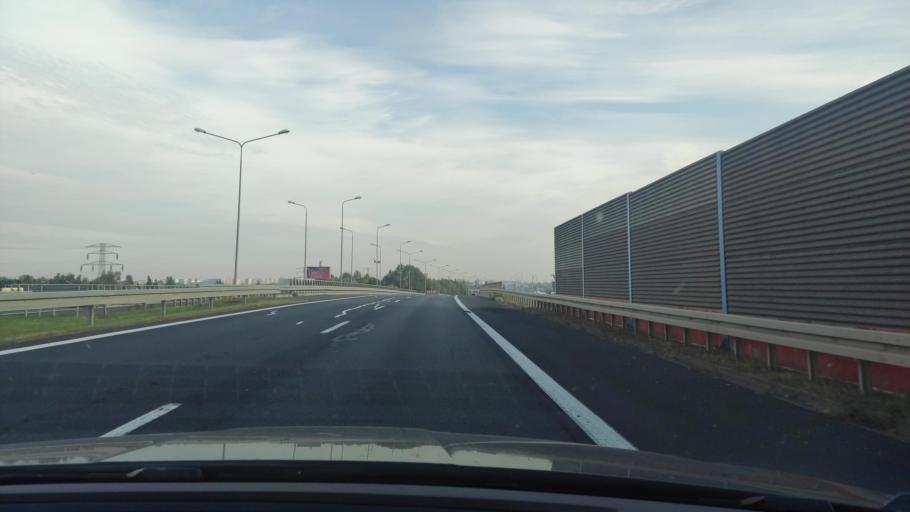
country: PL
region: Greater Poland Voivodeship
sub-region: Powiat poznanski
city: Plewiska
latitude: 52.3609
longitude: 16.8519
